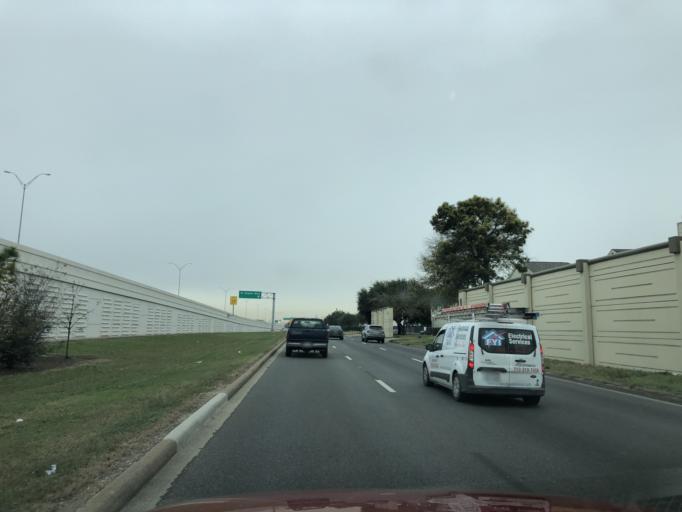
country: US
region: Texas
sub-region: Fort Bend County
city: Missouri City
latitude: 29.6383
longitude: -95.5317
